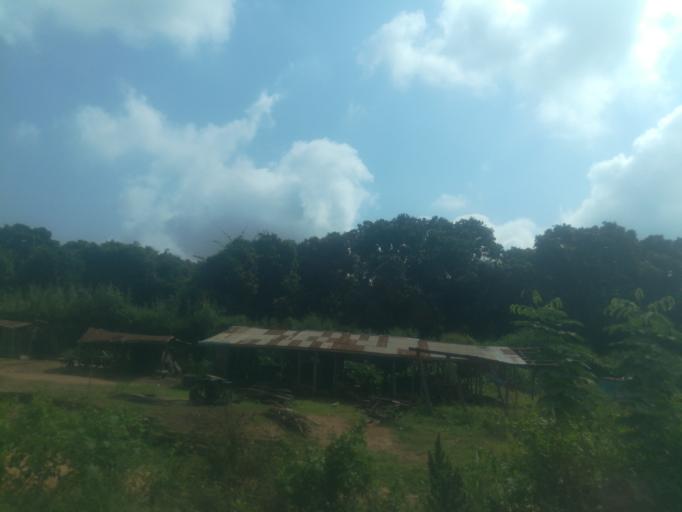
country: NG
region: Oyo
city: Moniya
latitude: 7.5315
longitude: 3.9168
